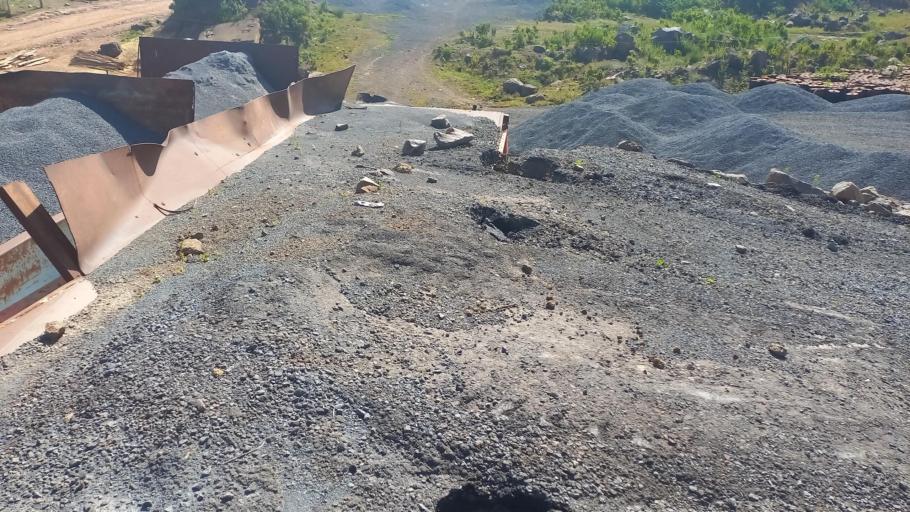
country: ET
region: Southern Nations, Nationalities, and People's Region
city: K'olito
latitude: 7.5398
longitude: 37.8441
